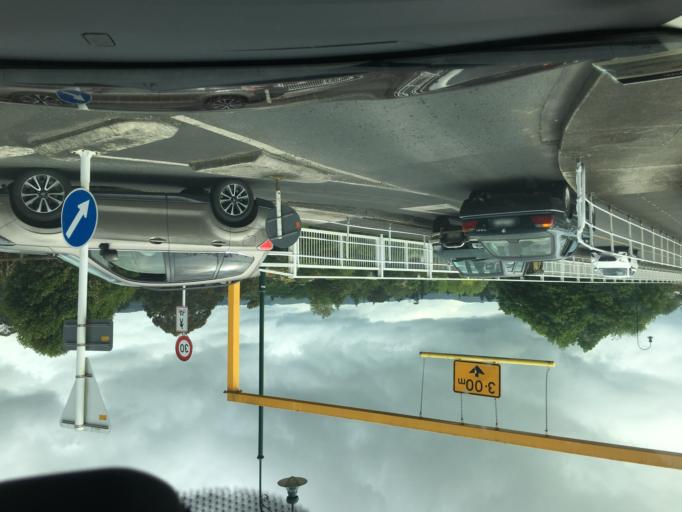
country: NZ
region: Waikato
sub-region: Waipa District
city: Cambridge
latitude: -37.9000
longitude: 175.4743
